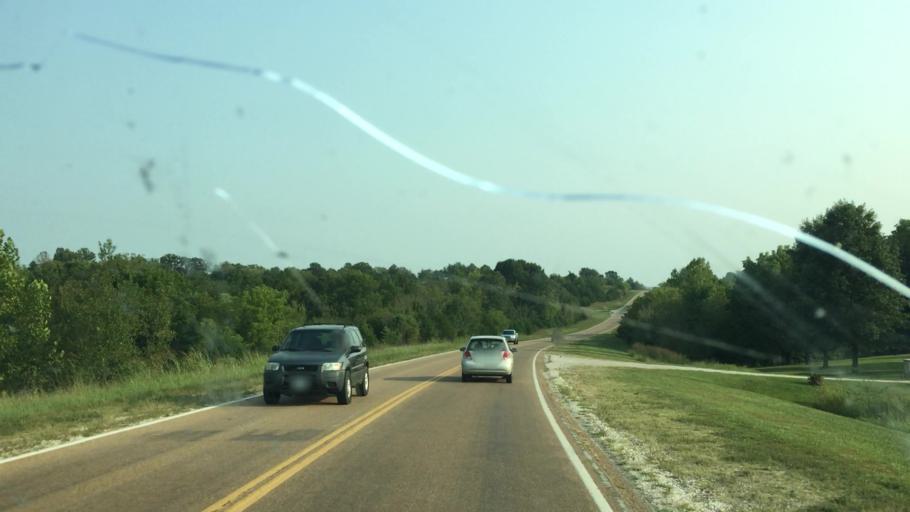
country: US
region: Missouri
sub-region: Pulaski County
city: Richland
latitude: 37.8368
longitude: -92.4072
